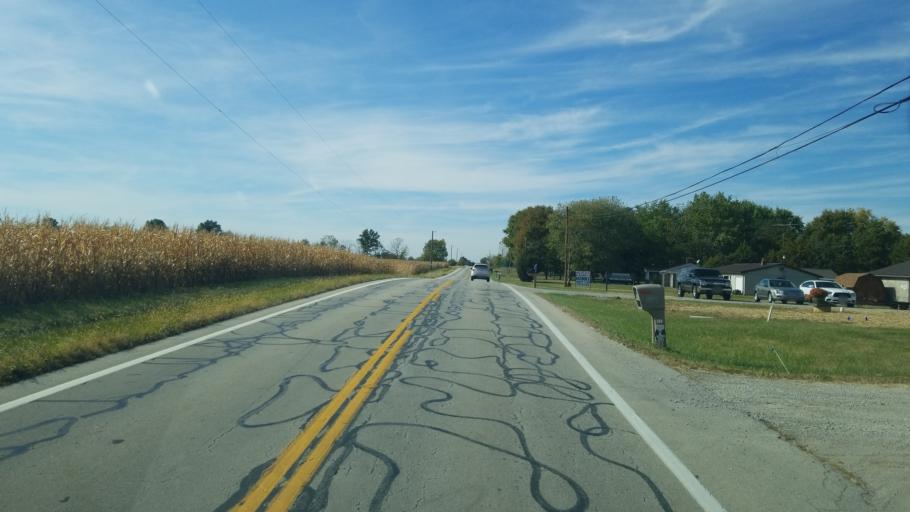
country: US
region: Ohio
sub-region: Clinton County
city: Wilmington
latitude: 39.3701
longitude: -83.8911
